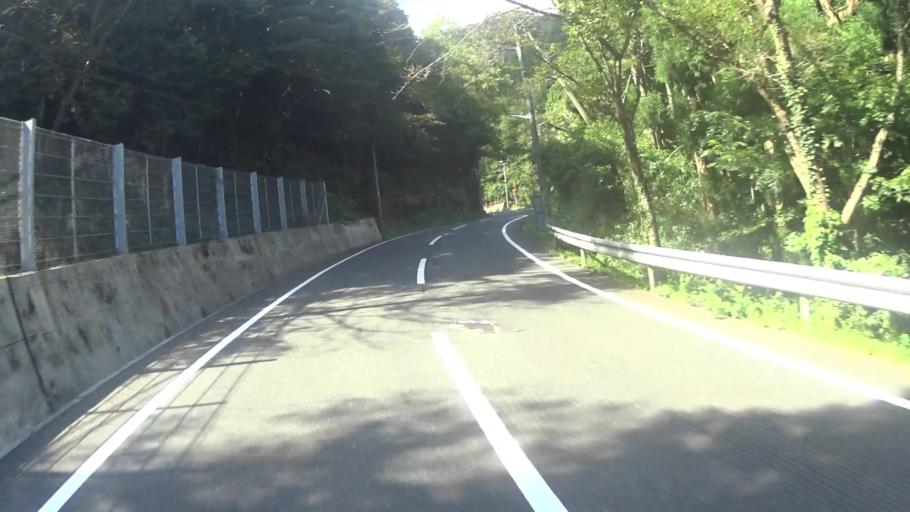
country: JP
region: Kyoto
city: Miyazu
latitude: 35.7073
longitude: 135.2769
